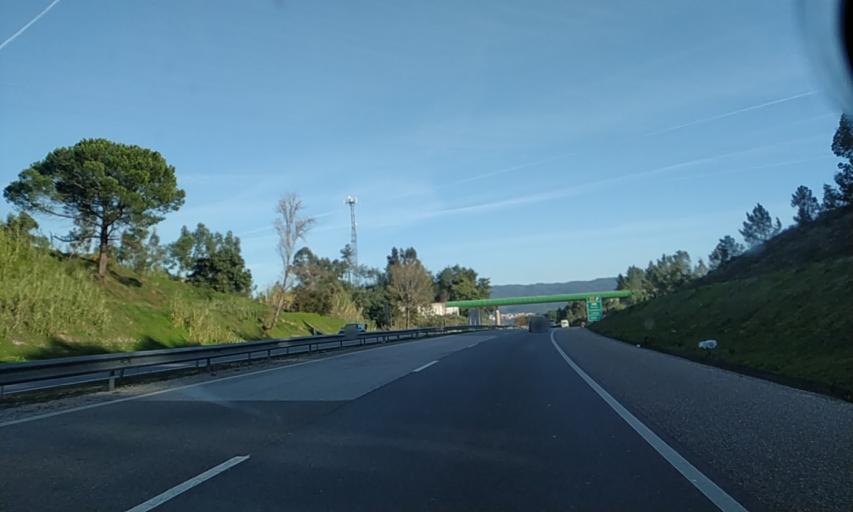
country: PT
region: Aveiro
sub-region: Mealhada
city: Pampilhosa do Botao
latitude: 40.2704
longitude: -8.4587
